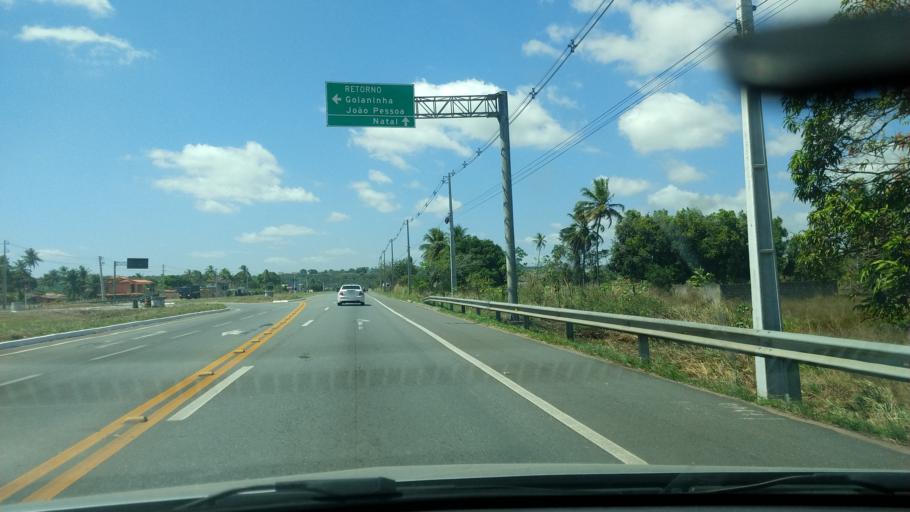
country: BR
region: Rio Grande do Norte
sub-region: Goianinha
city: Goianinha
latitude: -6.2510
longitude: -35.2155
